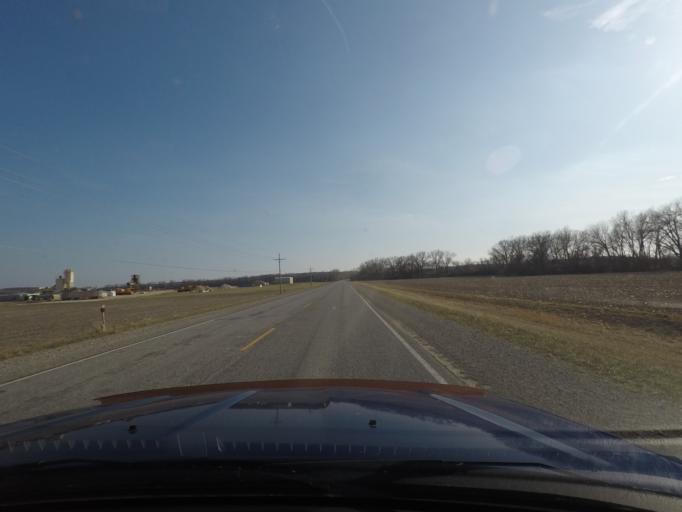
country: US
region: Kansas
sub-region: Jefferson County
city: Oskaloosa
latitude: 39.0596
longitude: -95.3826
